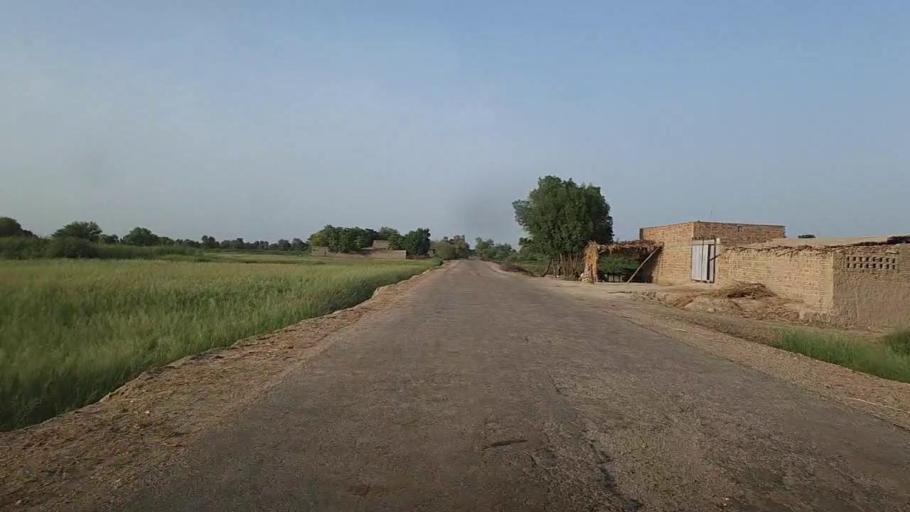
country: PK
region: Sindh
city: Ubauro
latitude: 28.1248
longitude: 69.8289
